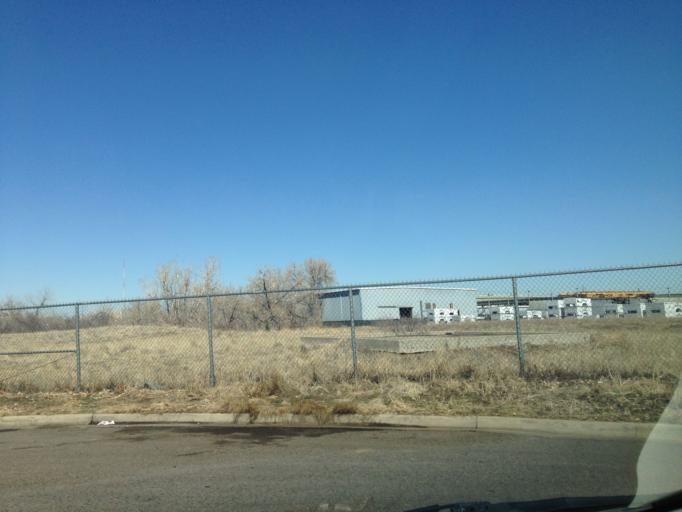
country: US
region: Colorado
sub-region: Adams County
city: Commerce City
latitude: 39.7924
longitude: -104.9720
